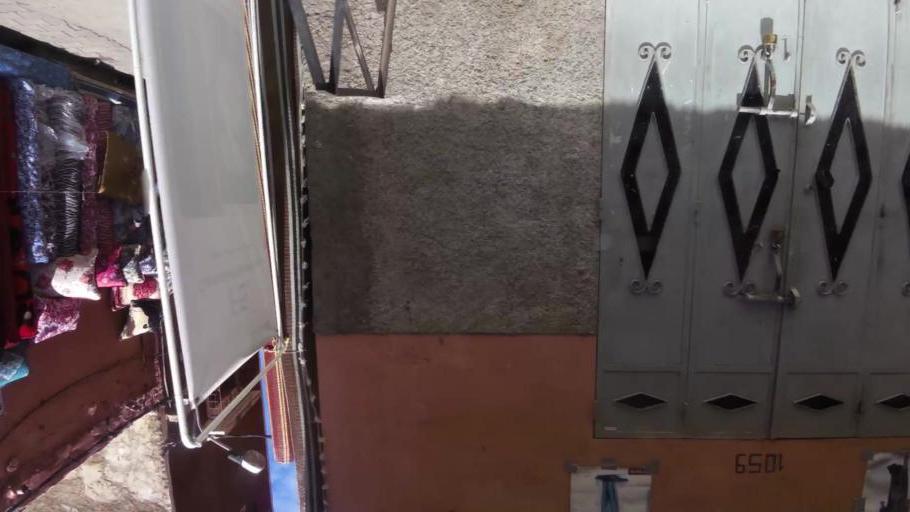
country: MA
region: Marrakech-Tensift-Al Haouz
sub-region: Marrakech
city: Marrakesh
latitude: 31.6184
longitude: -7.9696
